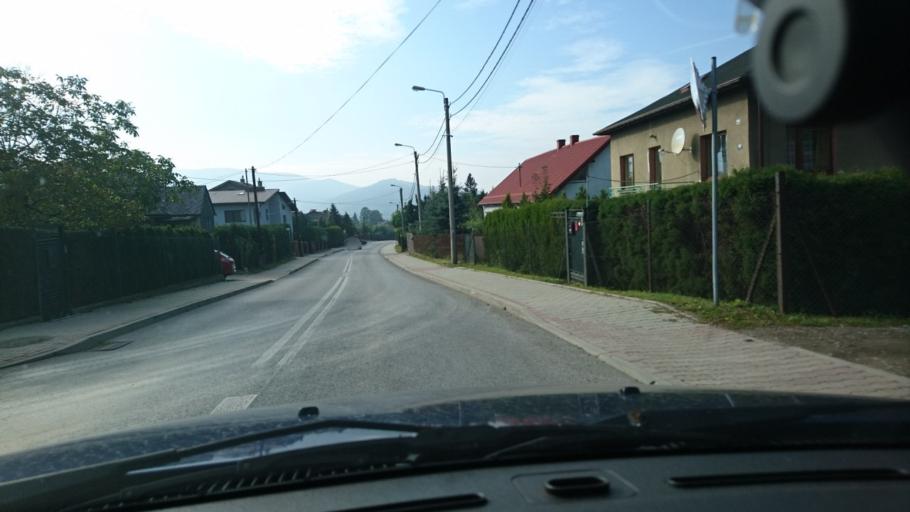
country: PL
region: Silesian Voivodeship
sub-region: Powiat bielski
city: Wilkowice
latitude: 49.7594
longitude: 19.1073
